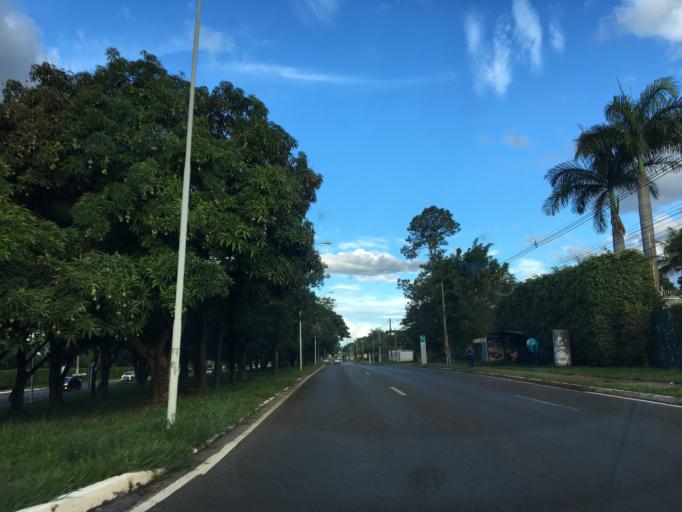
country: BR
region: Federal District
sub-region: Brasilia
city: Brasilia
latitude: -15.8579
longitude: -47.9241
